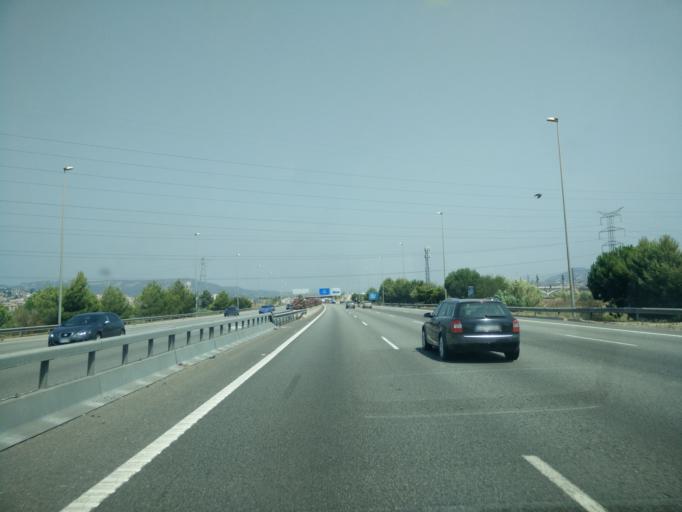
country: ES
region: Catalonia
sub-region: Provincia de Barcelona
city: Santa Coloma de Cervello
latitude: 41.3836
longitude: 2.0228
